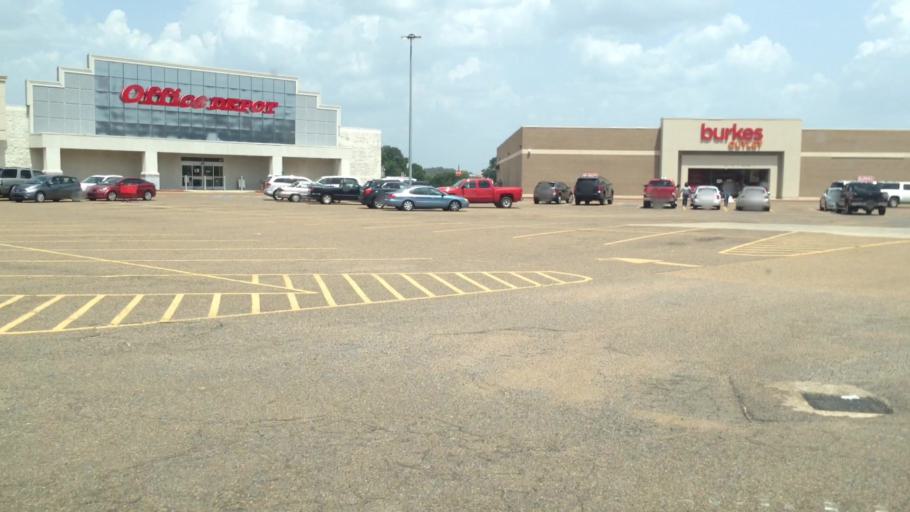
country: US
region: Louisiana
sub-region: Lincoln Parish
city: Ruston
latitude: 32.5416
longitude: -92.6359
